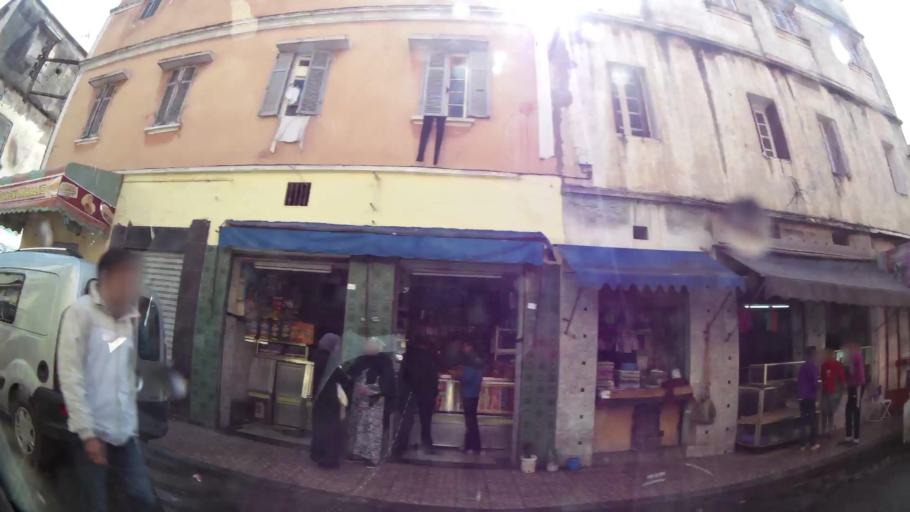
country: MA
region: Grand Casablanca
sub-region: Casablanca
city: Casablanca
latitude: 33.5760
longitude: -7.5920
